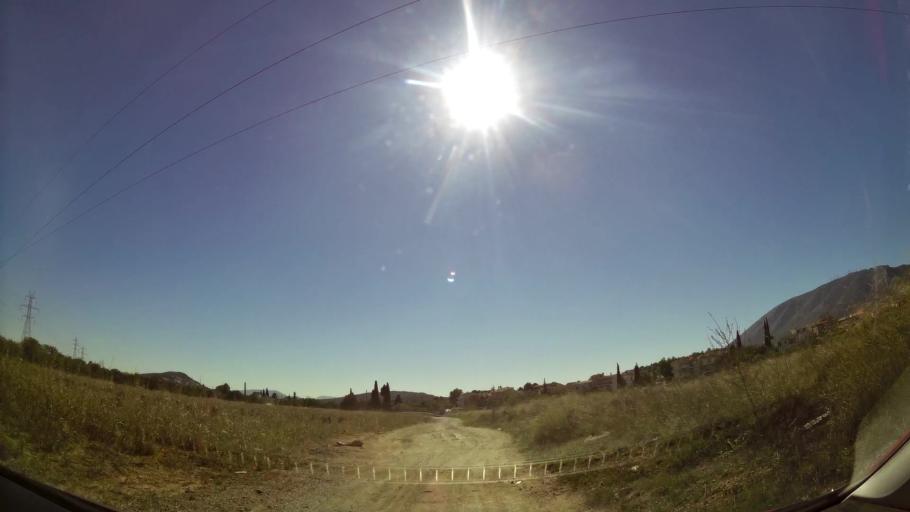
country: GR
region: Attica
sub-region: Nomarchia Anatolikis Attikis
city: Leondarion
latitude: 37.9942
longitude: 23.8631
